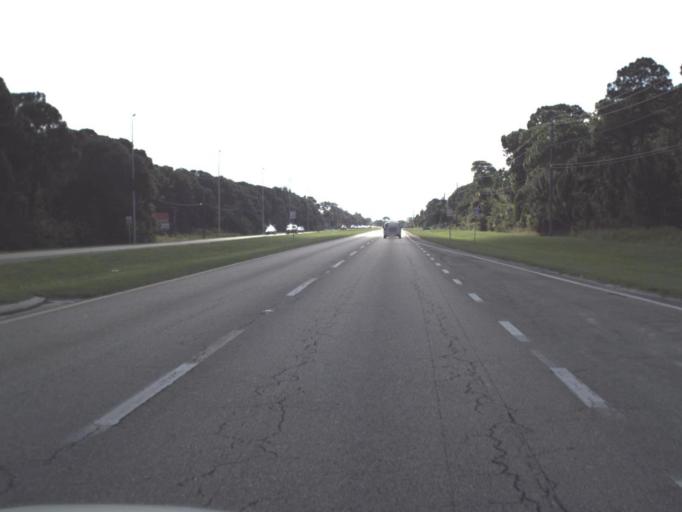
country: US
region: Florida
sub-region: Sarasota County
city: Gulf Gate Estates
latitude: 27.2402
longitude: -82.5056
